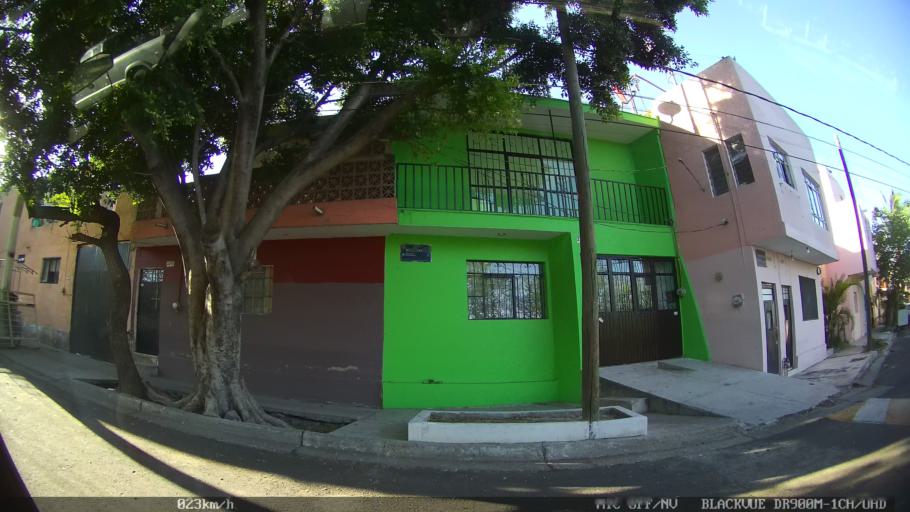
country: MX
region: Jalisco
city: Tlaquepaque
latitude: 20.7049
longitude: -103.2875
